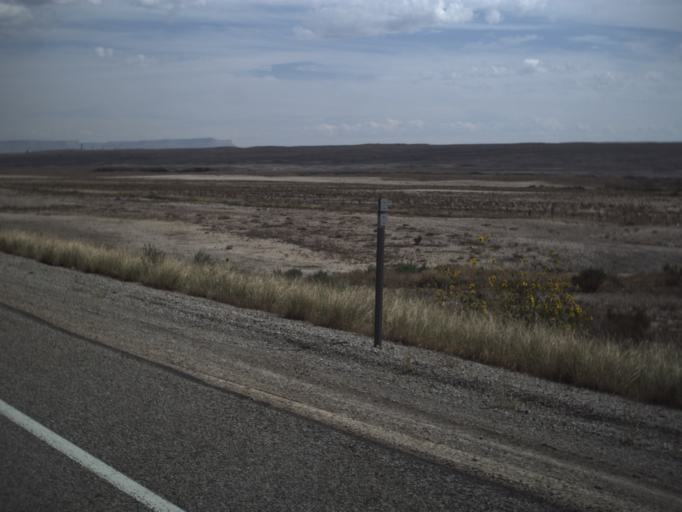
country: US
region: Utah
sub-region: Carbon County
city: East Carbon City
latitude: 38.9841
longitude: -110.2218
